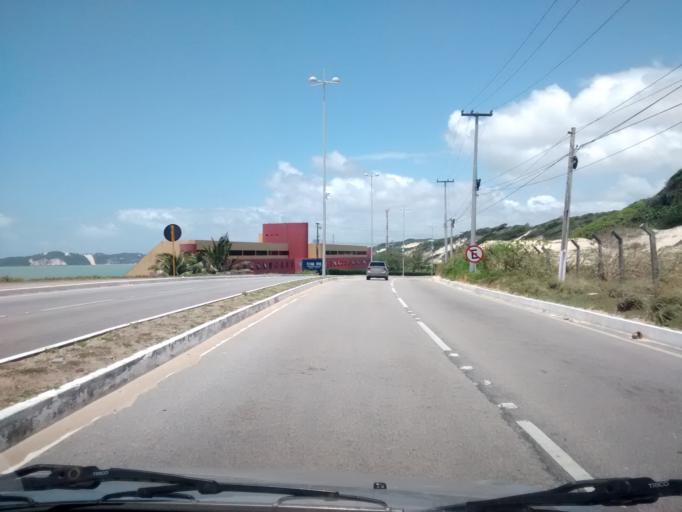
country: BR
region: Rio Grande do Norte
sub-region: Natal
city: Natal
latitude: -5.8398
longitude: -35.1821
